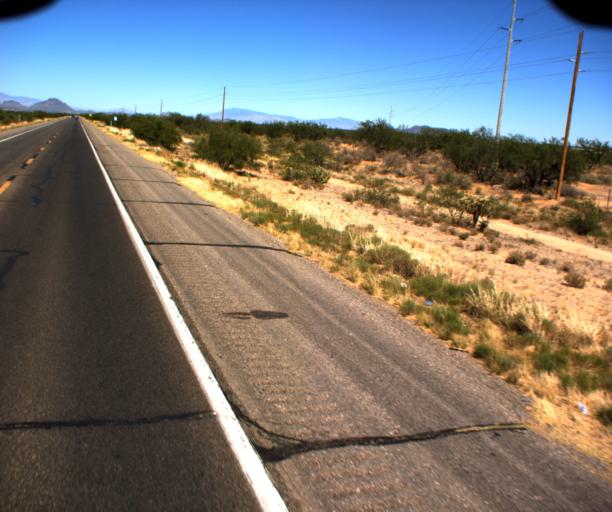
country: US
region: Arizona
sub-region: Pima County
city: Three Points
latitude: 32.1040
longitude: -111.2450
